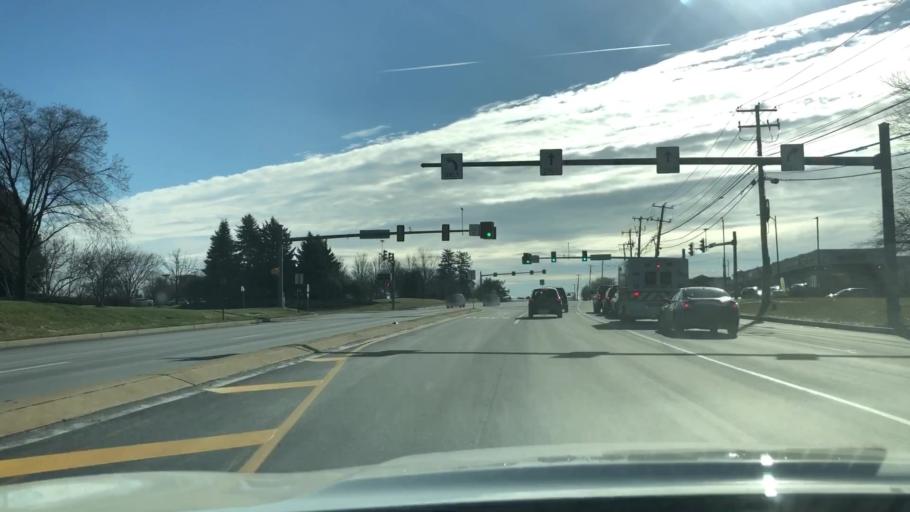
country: US
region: Pennsylvania
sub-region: Lehigh County
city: Catasauqua
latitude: 40.6583
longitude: -75.4190
